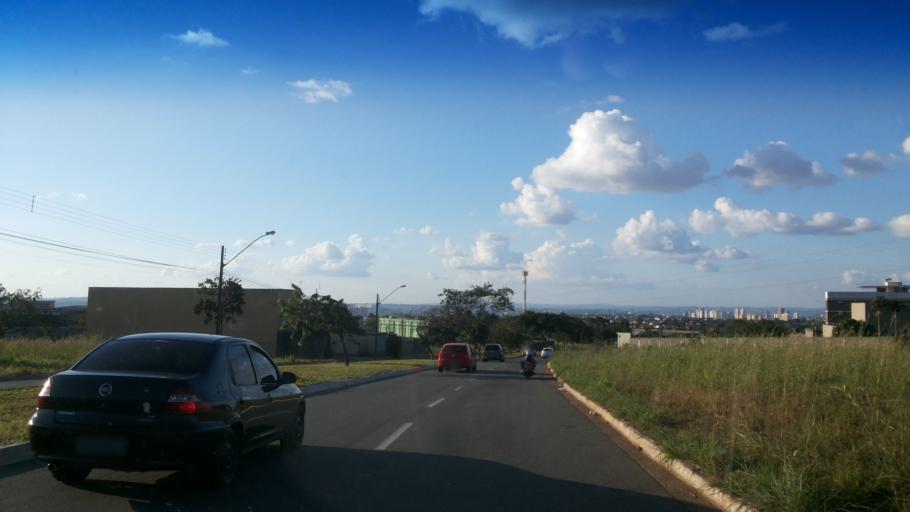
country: BR
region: Goias
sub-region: Goiania
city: Goiania
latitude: -16.7492
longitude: -49.3194
